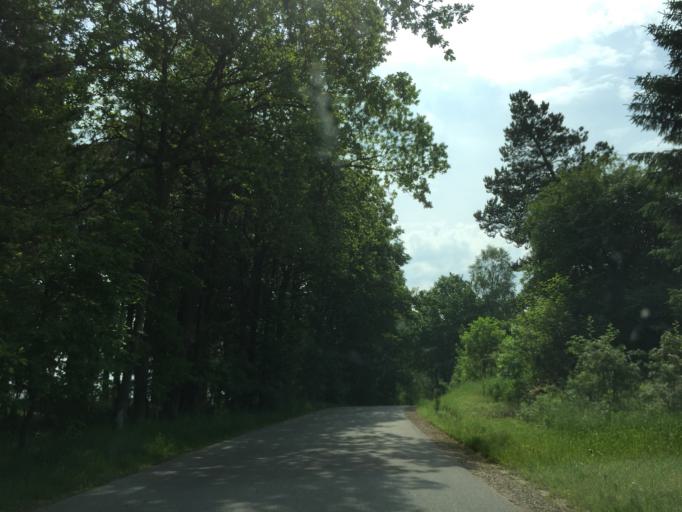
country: DK
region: Central Jutland
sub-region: Silkeborg Kommune
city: Virklund
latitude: 56.0476
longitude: 9.4555
